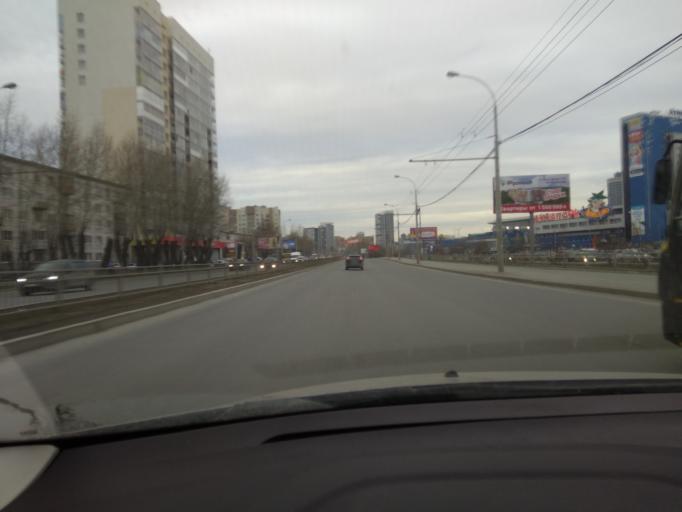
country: RU
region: Sverdlovsk
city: Yekaterinburg
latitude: 56.7883
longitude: 60.6471
